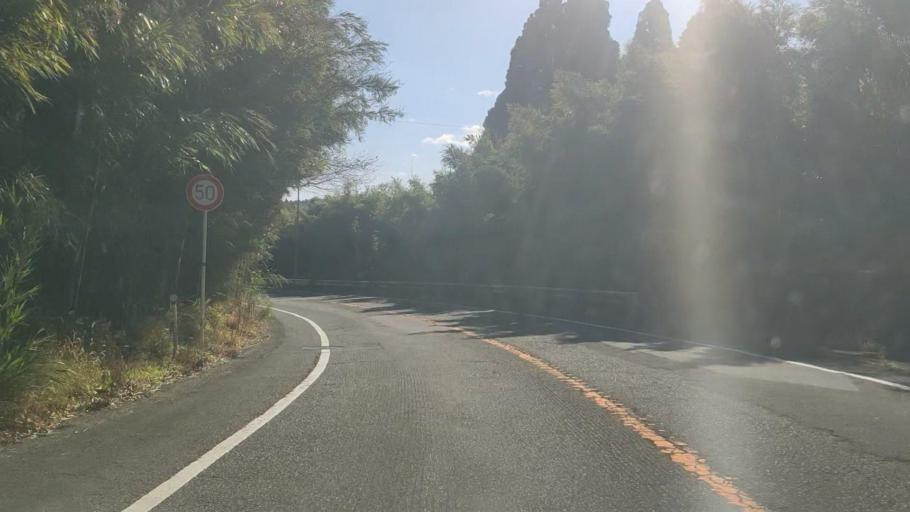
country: JP
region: Kagoshima
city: Kokubu-matsuki
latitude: 31.6637
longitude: 130.8816
